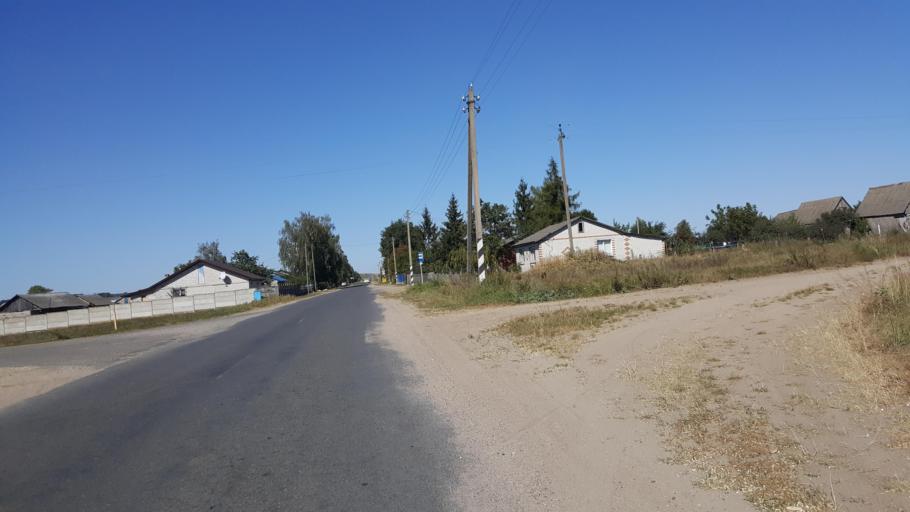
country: PL
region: Lublin Voivodeship
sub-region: Powiat bialski
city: Rokitno
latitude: 52.2402
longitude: 23.3393
